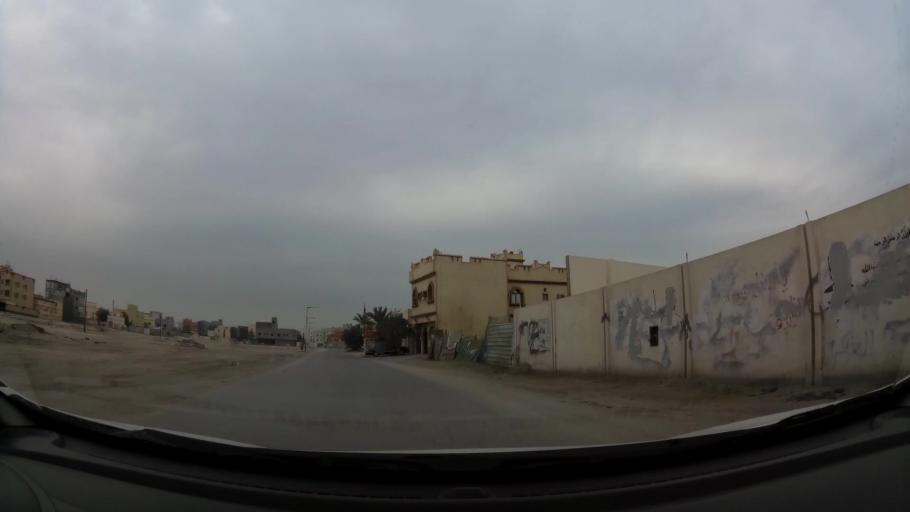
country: BH
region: Northern
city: Sitrah
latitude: 26.1406
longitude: 50.6093
